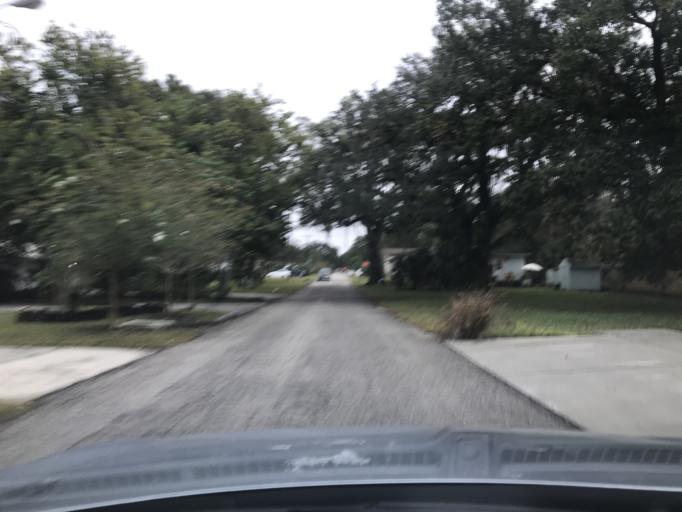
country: US
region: Florida
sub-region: Hillsborough County
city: Tampa
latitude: 27.9852
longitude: -82.4663
